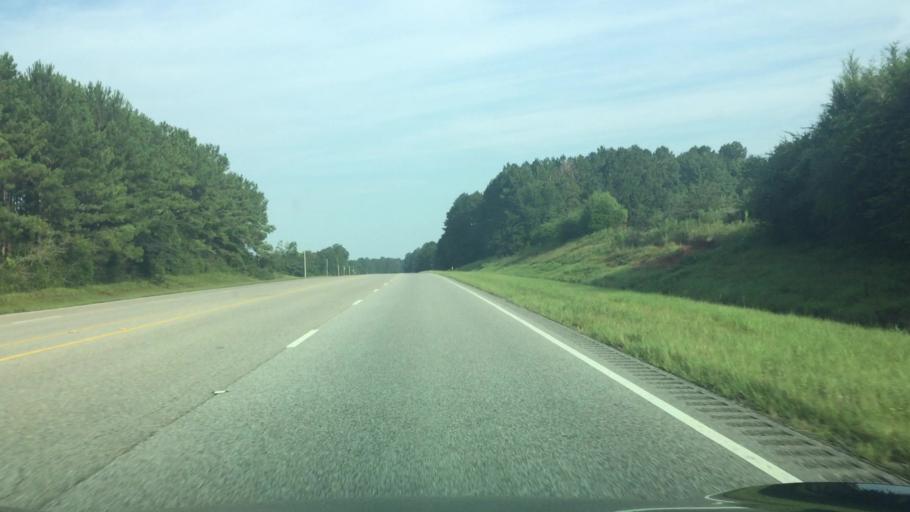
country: US
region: Alabama
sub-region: Covington County
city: Andalusia
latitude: 31.4022
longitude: -86.5887
